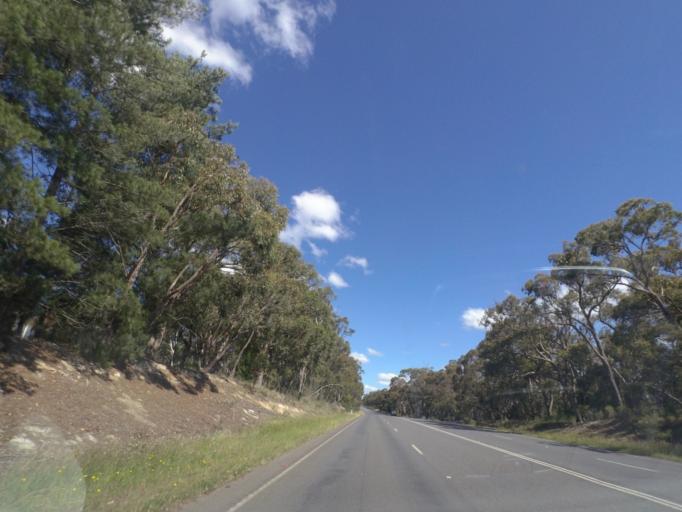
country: AU
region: Victoria
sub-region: Hume
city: Sunbury
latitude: -37.4417
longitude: 144.5668
